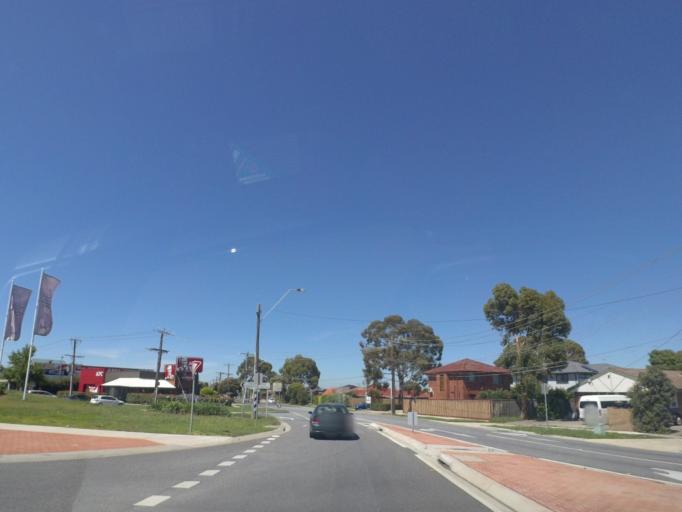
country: AU
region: Victoria
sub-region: Hume
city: Tullamarine
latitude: -37.6997
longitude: 144.8803
